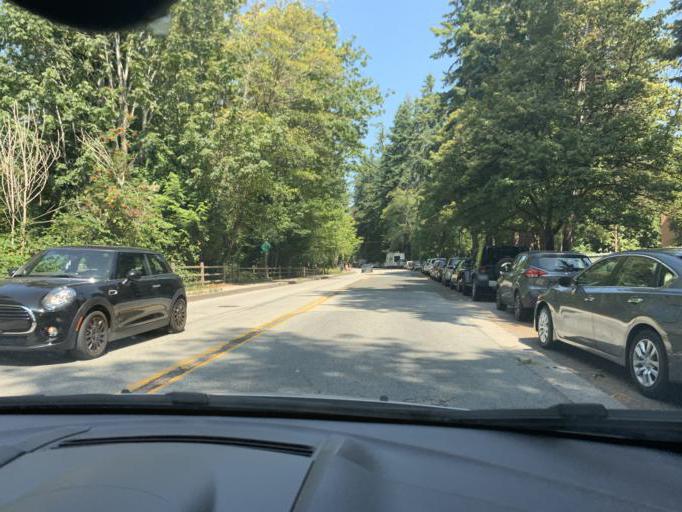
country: CA
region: British Columbia
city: West End
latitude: 49.2647
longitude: -123.2606
